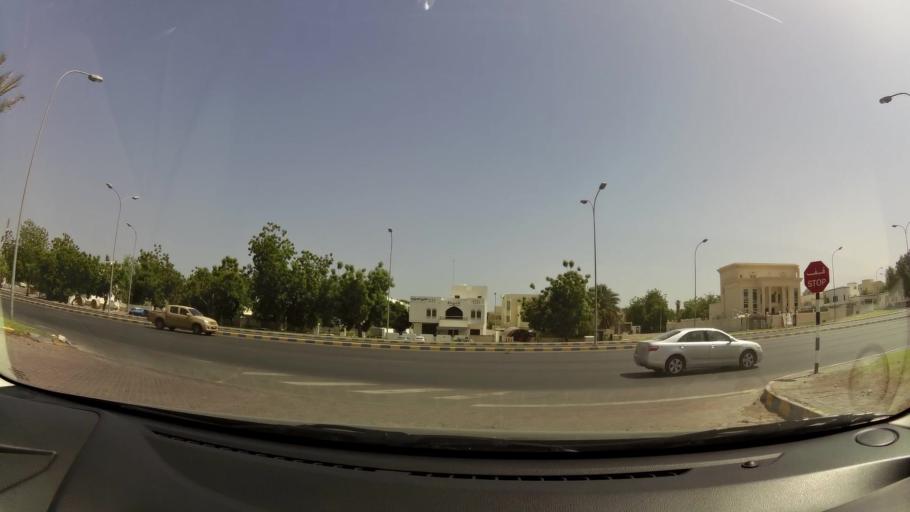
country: OM
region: Muhafazat Masqat
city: Bawshar
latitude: 23.5970
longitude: 58.4485
